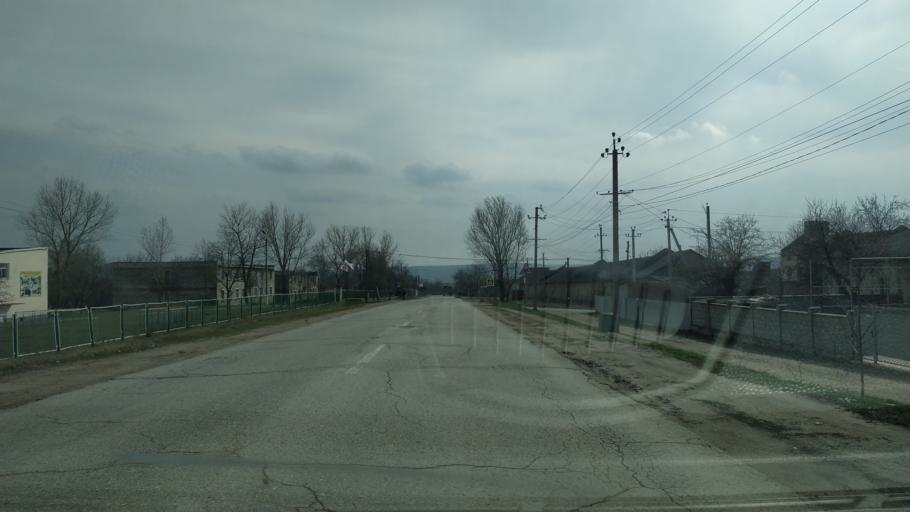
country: MD
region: Gagauzia
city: Vulcanesti
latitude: 45.6964
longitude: 28.4039
